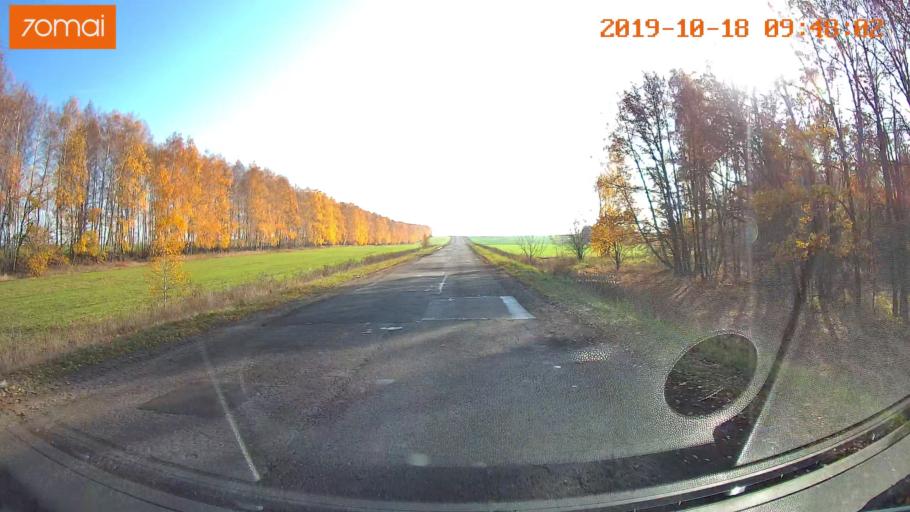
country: RU
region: Tula
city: Kazachka
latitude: 53.3196
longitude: 38.2407
